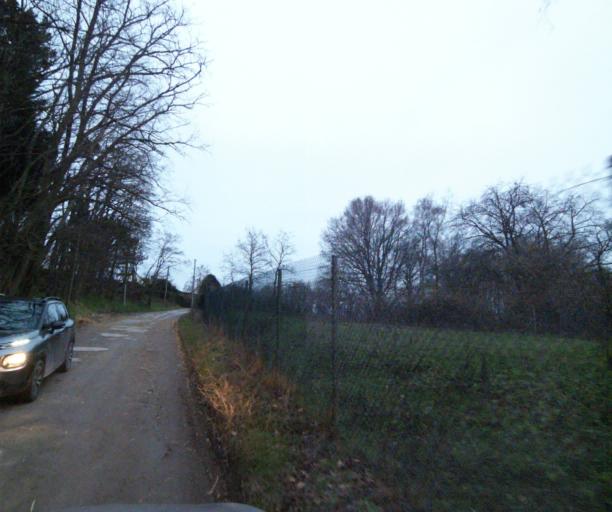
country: FR
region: Ile-de-France
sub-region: Departement de Seine-et-Marne
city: Longperrier
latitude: 49.0606
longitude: 2.6621
